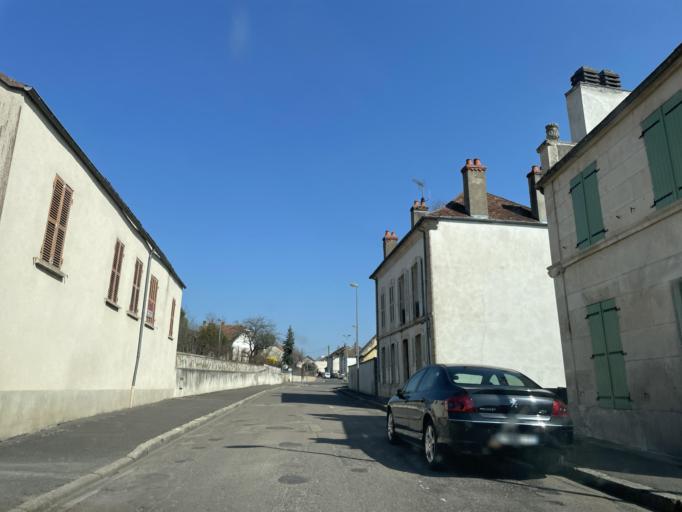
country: FR
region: Bourgogne
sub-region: Departement de la Cote-d'Or
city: Semur-en-Auxois
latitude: 47.4898
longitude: 4.3388
